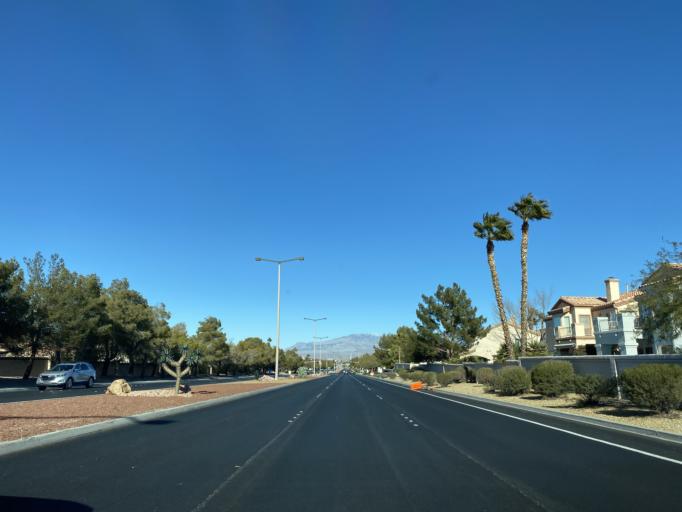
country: US
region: Nevada
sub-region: Clark County
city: Summerlin South
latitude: 36.2073
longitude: -115.2789
